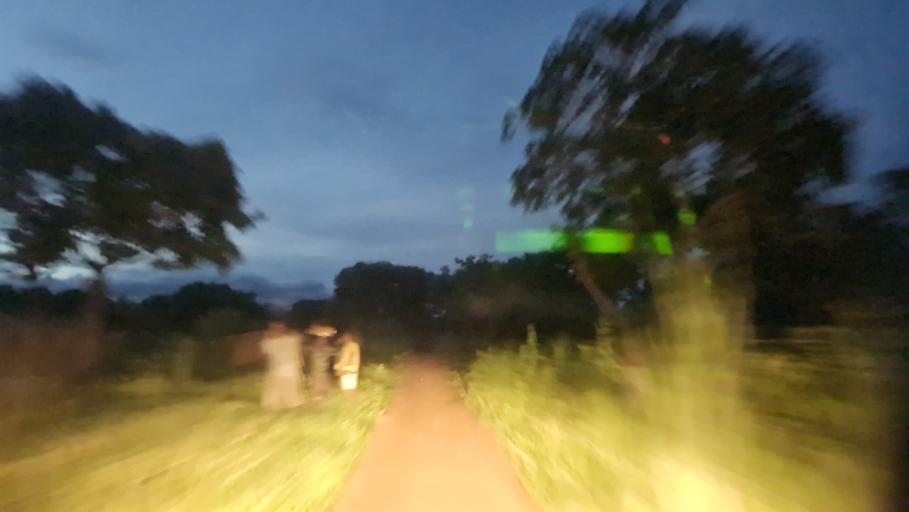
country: MZ
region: Nampula
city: Nampula
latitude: -14.6793
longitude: 39.8319
